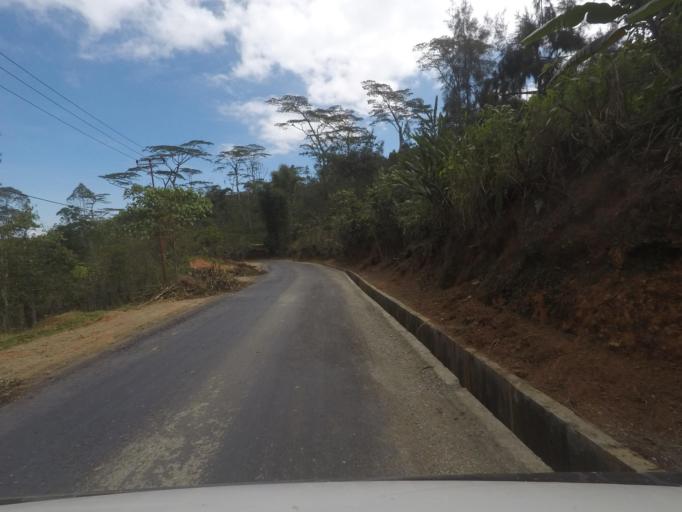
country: TL
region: Ermera
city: Gleno
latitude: -8.7465
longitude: 125.3498
